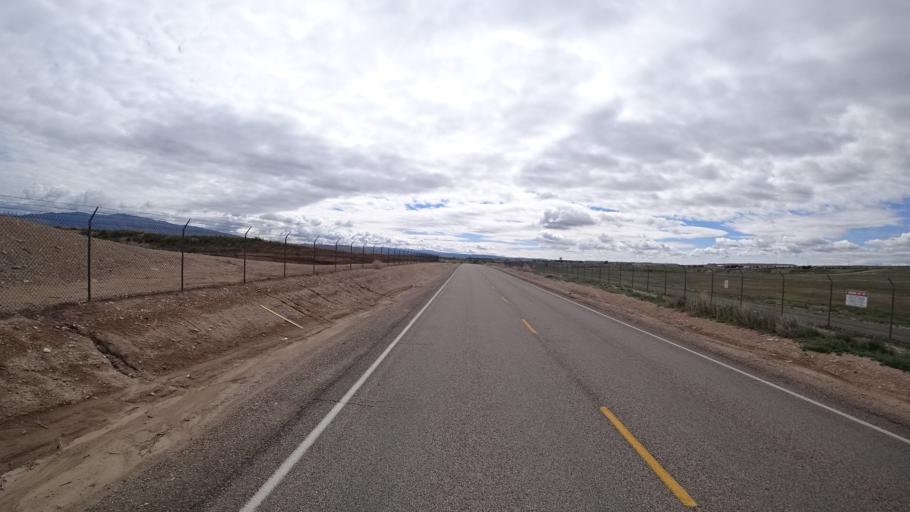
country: US
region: Idaho
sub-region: Ada County
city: Boise
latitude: 43.5556
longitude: -116.1899
